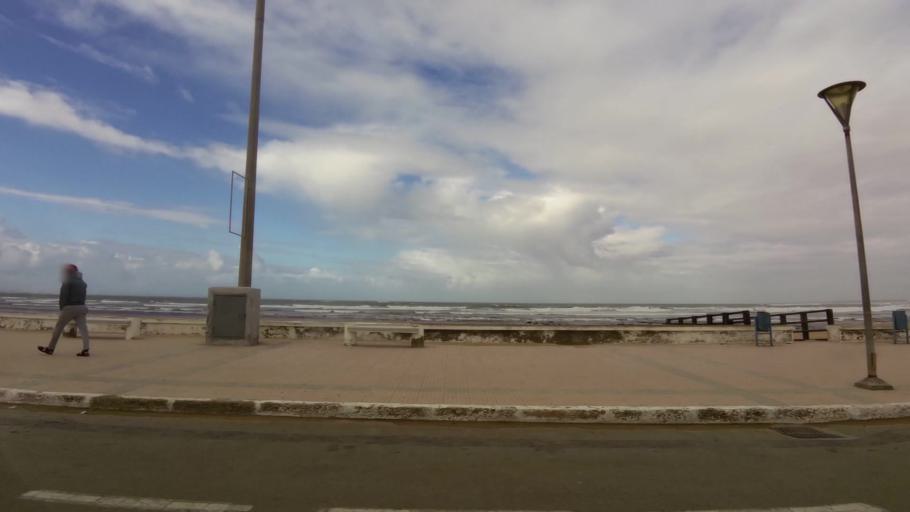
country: MA
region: Doukkala-Abda
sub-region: El-Jadida
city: El Jadida
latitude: 33.2457
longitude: -8.4913
